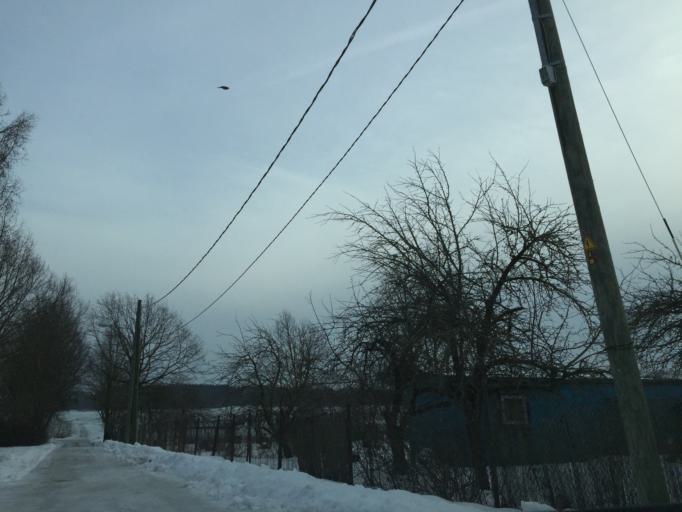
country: LV
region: Salaspils
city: Salaspils
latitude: 56.8427
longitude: 24.4314
